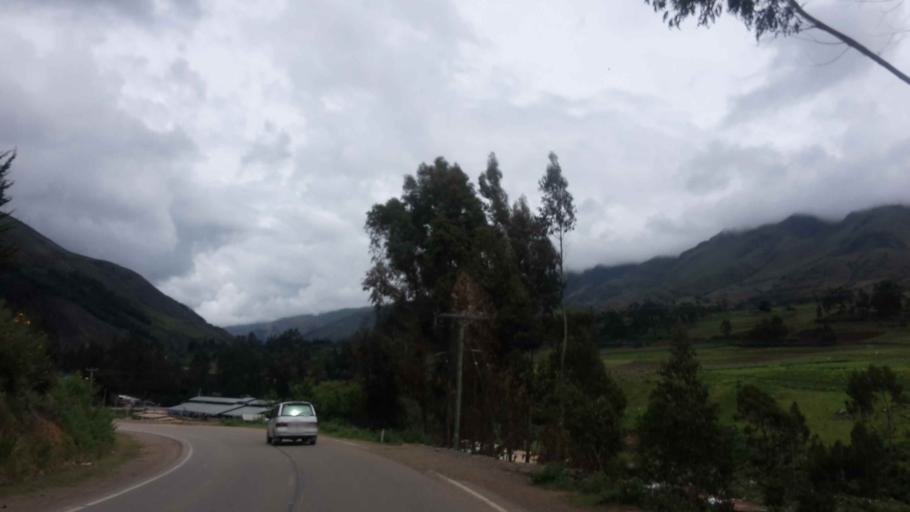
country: BO
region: Cochabamba
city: Totora
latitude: -17.5333
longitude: -65.3746
